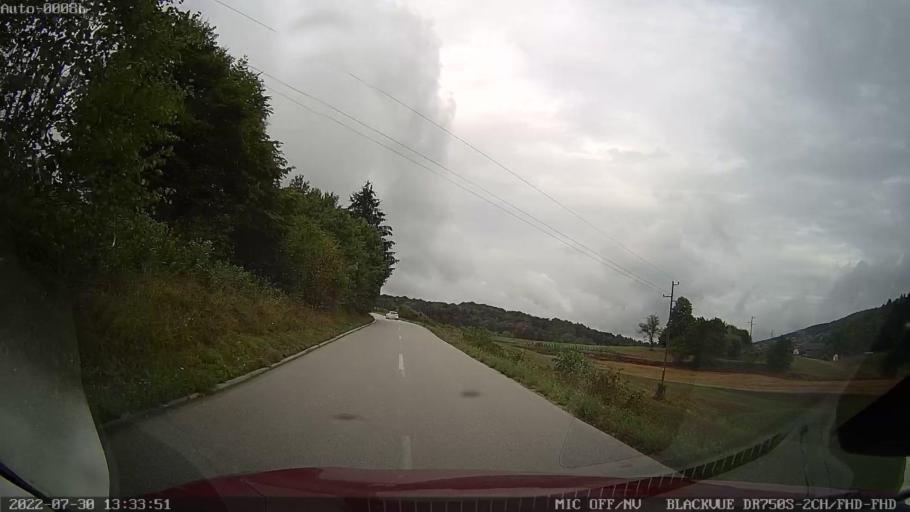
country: SI
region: Zuzemberk
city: Zuzemberk
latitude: 45.8542
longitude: 14.9344
